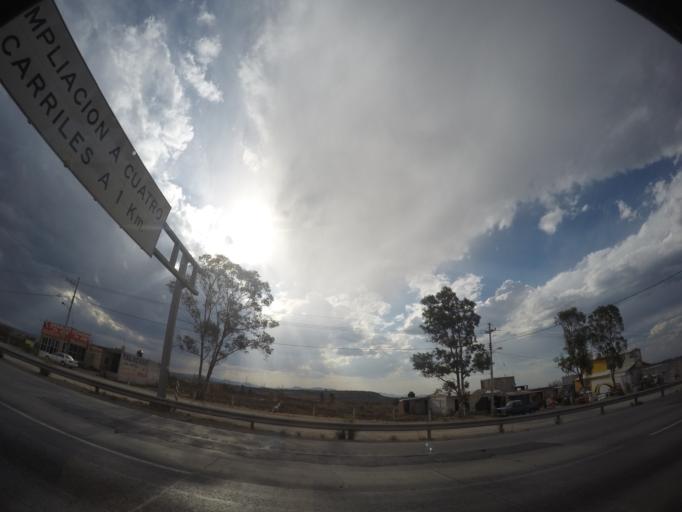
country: MX
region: Mexico
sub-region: Jilotepec
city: La Comunidad
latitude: 20.0585
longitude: -99.5947
